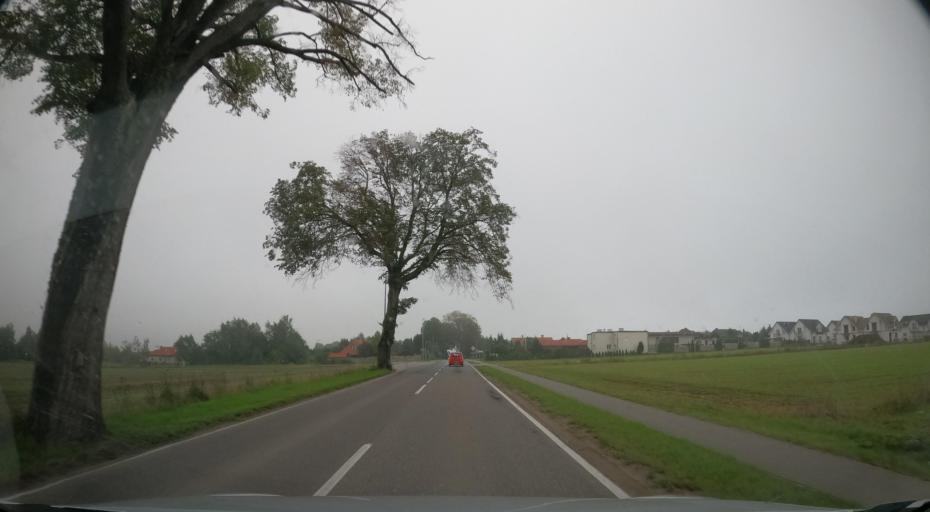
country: PL
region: Pomeranian Voivodeship
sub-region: Powiat wejherowski
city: Bojano
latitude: 54.4476
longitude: 18.3818
